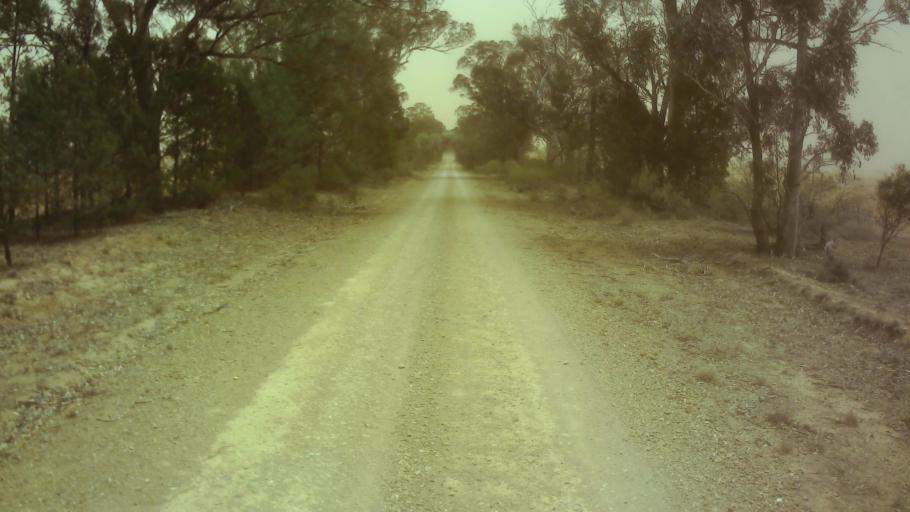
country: AU
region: New South Wales
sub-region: Weddin
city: Grenfell
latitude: -33.7084
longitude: 147.9423
